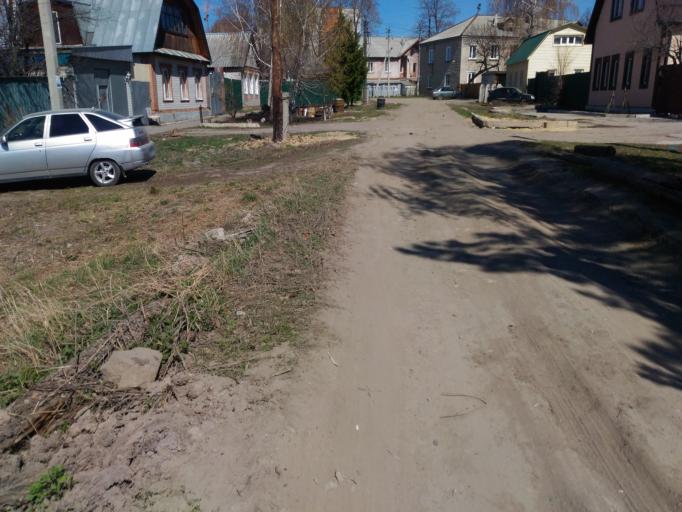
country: RU
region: Ulyanovsk
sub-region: Ulyanovskiy Rayon
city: Ulyanovsk
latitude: 54.3419
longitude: 48.3885
